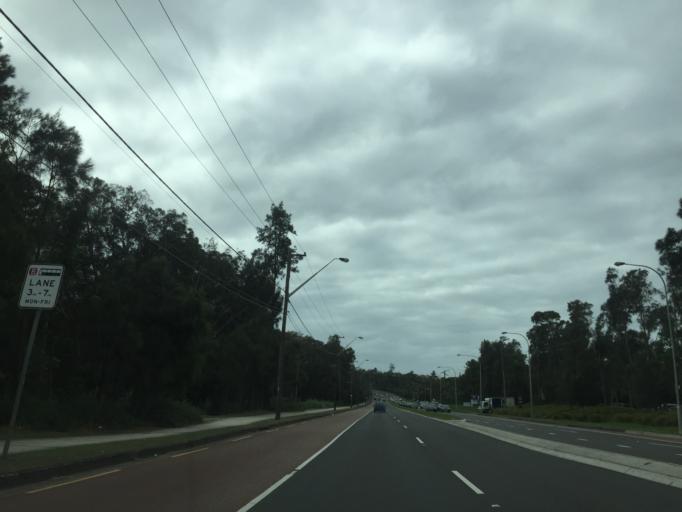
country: AU
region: New South Wales
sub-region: Pittwater
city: Warriewood
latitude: -33.6966
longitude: 151.3013
